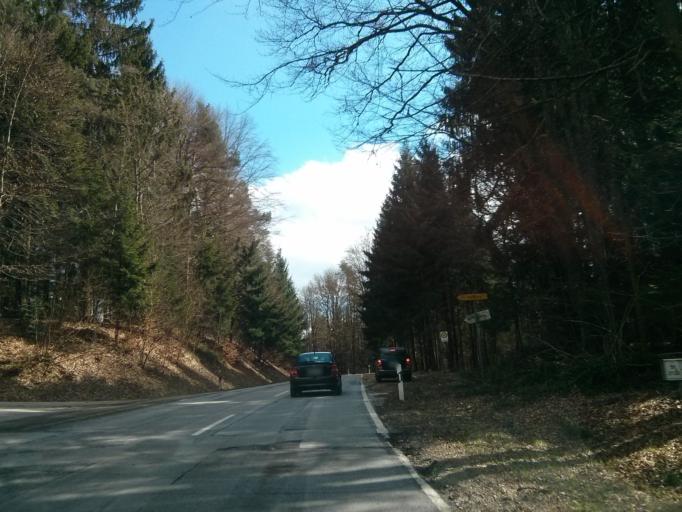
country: DE
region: Bavaria
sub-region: Lower Bavaria
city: Schaufling
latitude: 48.8415
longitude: 13.0423
